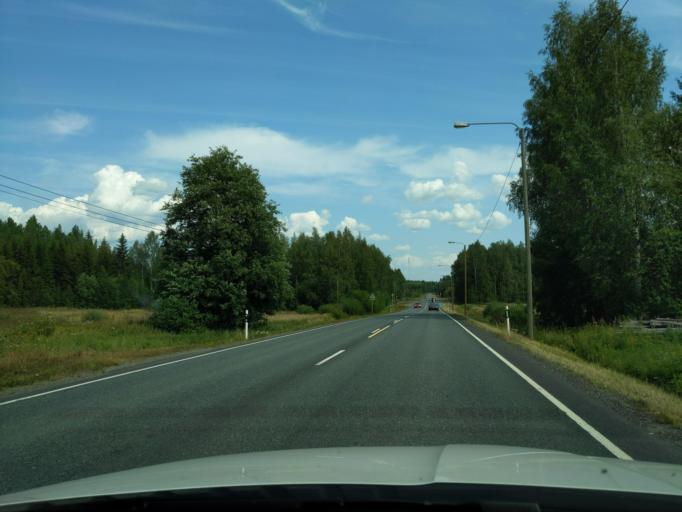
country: FI
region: Haeme
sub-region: Haemeenlinna
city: Tuulos
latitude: 61.0930
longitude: 24.8059
